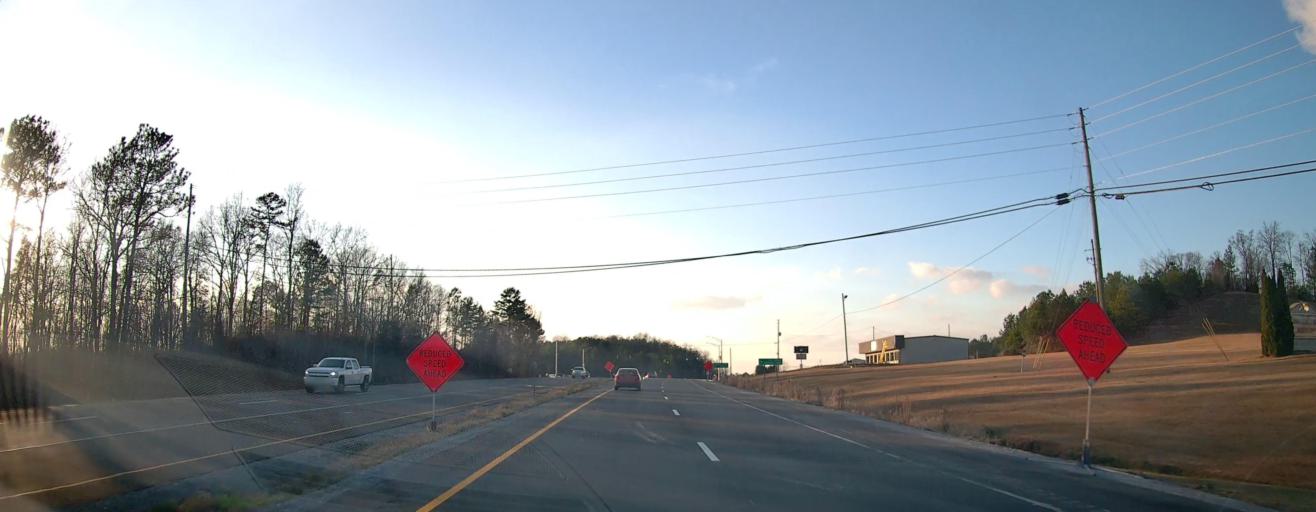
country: US
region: Alabama
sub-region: Calhoun County
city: Saks
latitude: 33.7170
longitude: -85.8654
